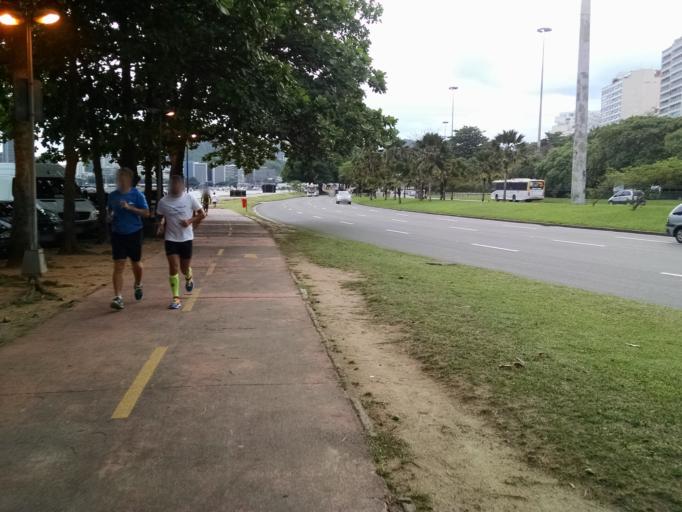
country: BR
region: Rio de Janeiro
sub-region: Rio De Janeiro
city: Rio de Janeiro
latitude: -22.9405
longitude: -43.1702
